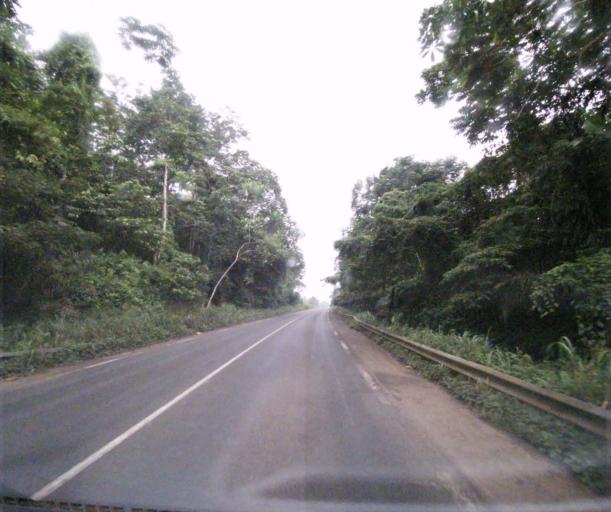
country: CM
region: Centre
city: Eseka
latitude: 3.8802
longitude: 10.6916
